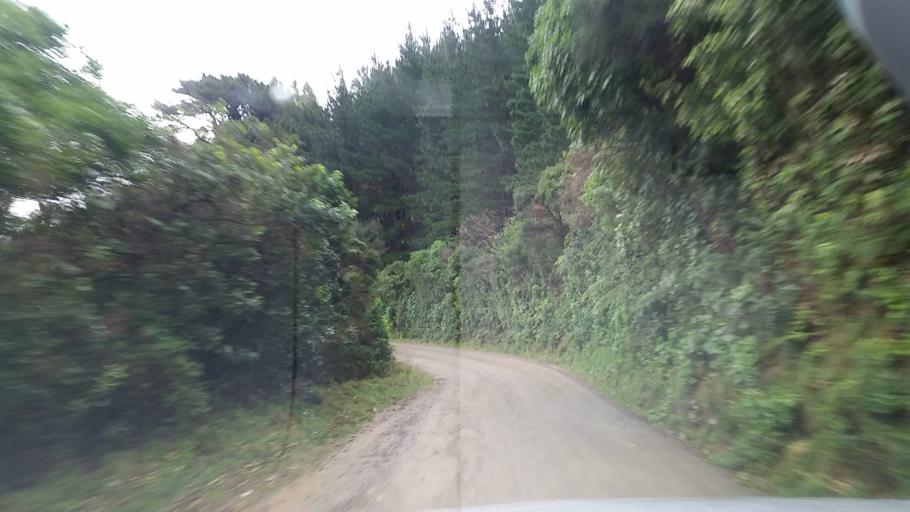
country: NZ
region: Marlborough
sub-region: Marlborough District
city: Picton
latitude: -41.1750
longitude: 174.0435
